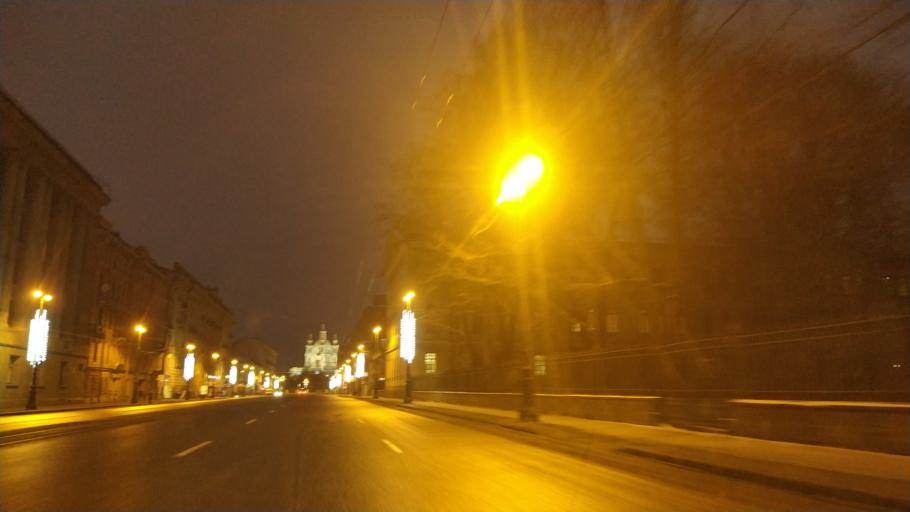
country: RU
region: St.-Petersburg
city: Centralniy
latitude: 59.9433
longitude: 30.3843
